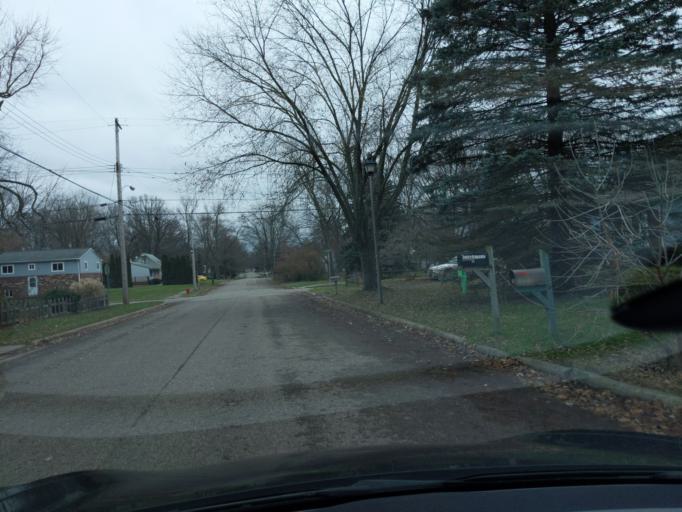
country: US
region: Michigan
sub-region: Ingham County
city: Lansing
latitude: 42.7025
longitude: -84.5872
